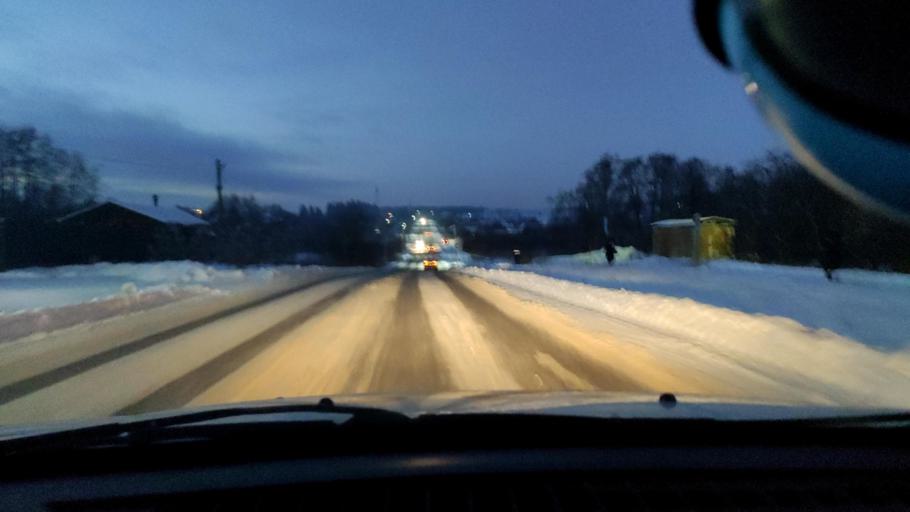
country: RU
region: Perm
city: Kultayevo
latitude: 57.8982
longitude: 55.9284
